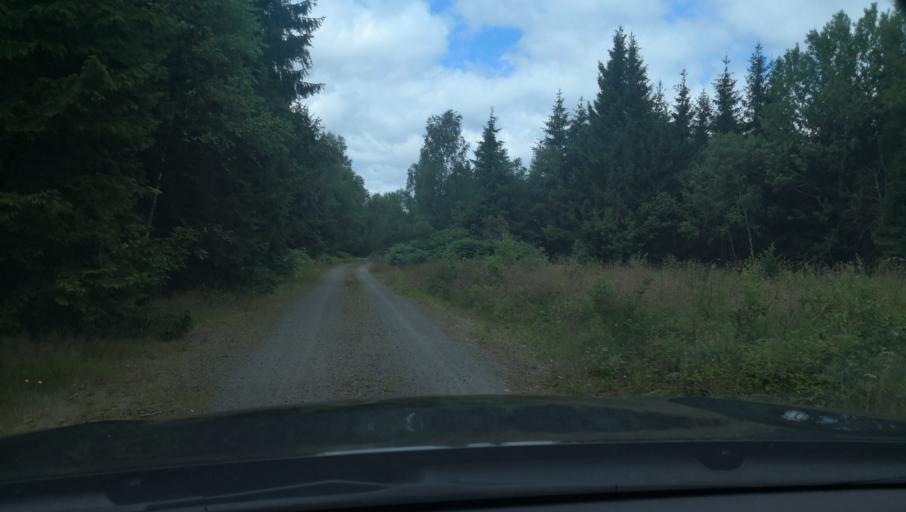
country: SE
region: Skane
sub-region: Simrishamns Kommun
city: Kivik
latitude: 55.6112
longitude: 14.1075
